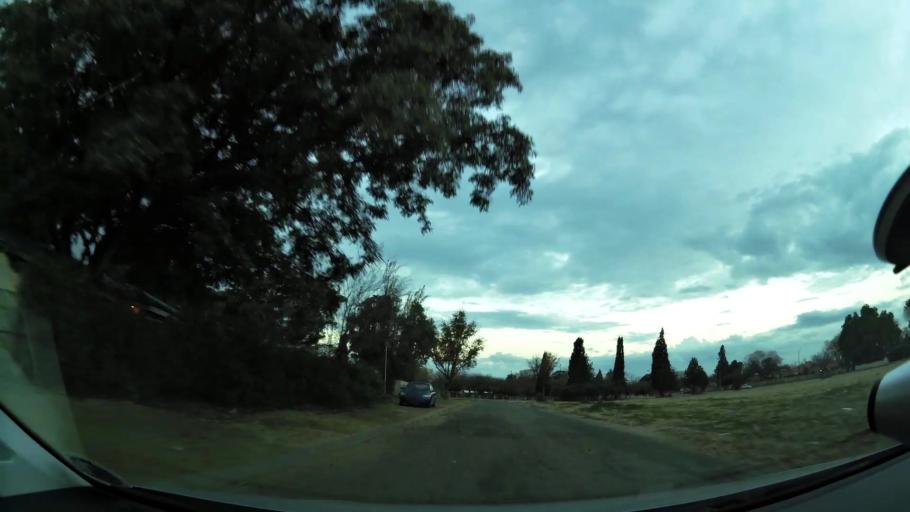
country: ZA
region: Orange Free State
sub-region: Lejweleputswa District Municipality
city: Welkom
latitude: -27.9785
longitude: 26.7502
